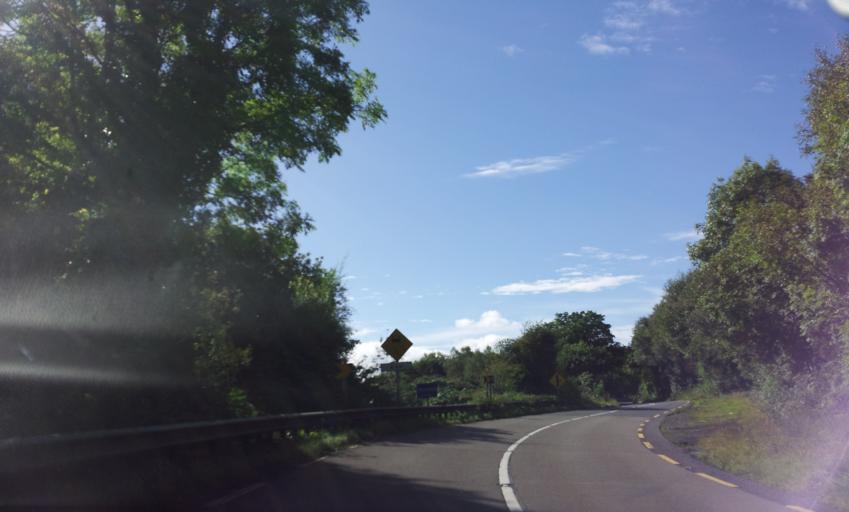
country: IE
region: Munster
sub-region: County Cork
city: Macroom
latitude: 51.9183
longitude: -9.0713
